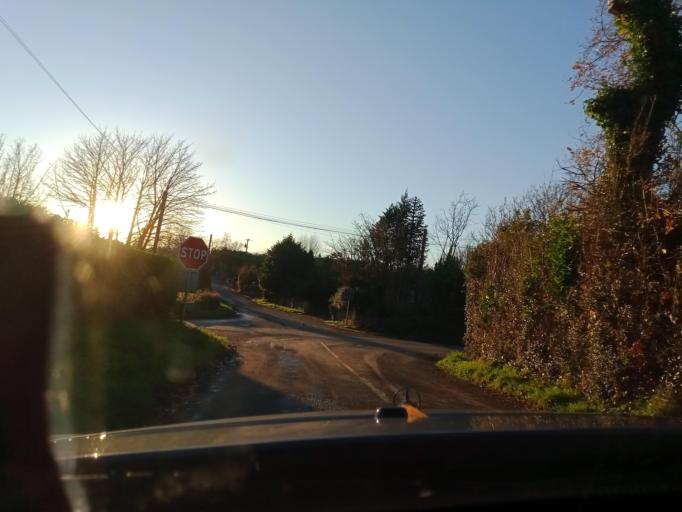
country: IE
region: Leinster
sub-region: Loch Garman
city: New Ross
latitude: 52.3819
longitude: -7.0061
